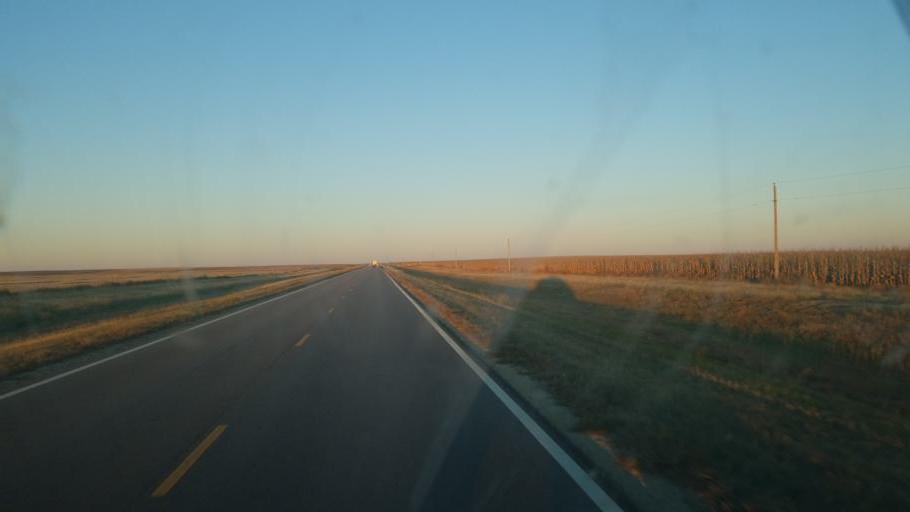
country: US
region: Kansas
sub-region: Wallace County
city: Sharon Springs
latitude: 38.9015
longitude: -101.7852
